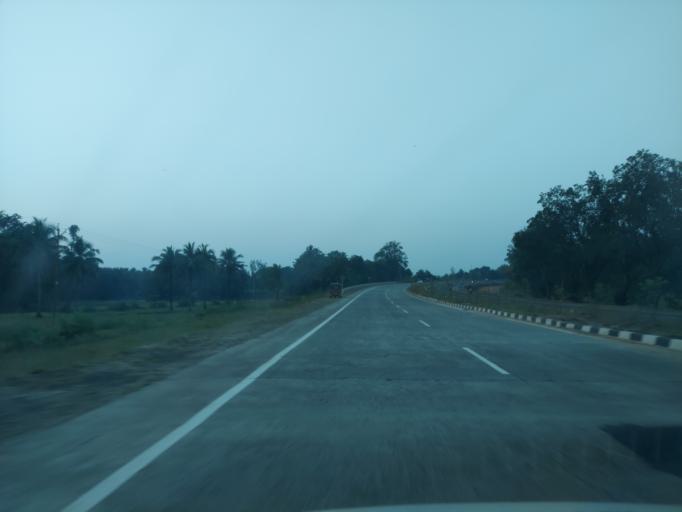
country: IN
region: Maharashtra
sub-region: Sindhudurg
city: Kudal
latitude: 16.0912
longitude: 73.7069
